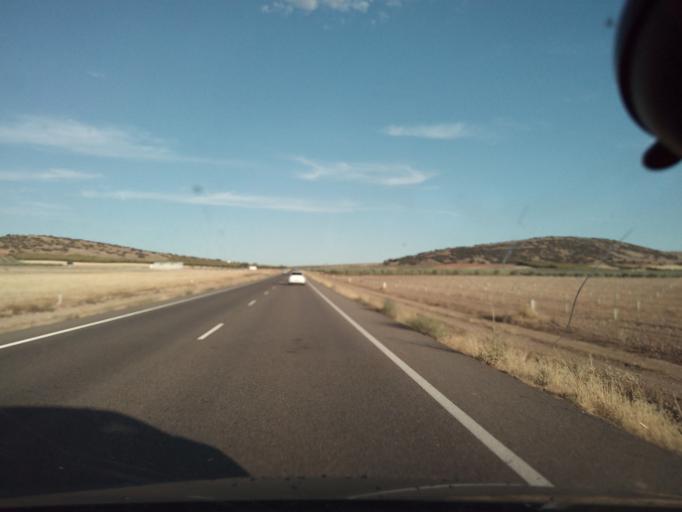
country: ES
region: Castille-La Mancha
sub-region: Province of Toledo
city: Tembleque
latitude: 39.6565
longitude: -3.4469
